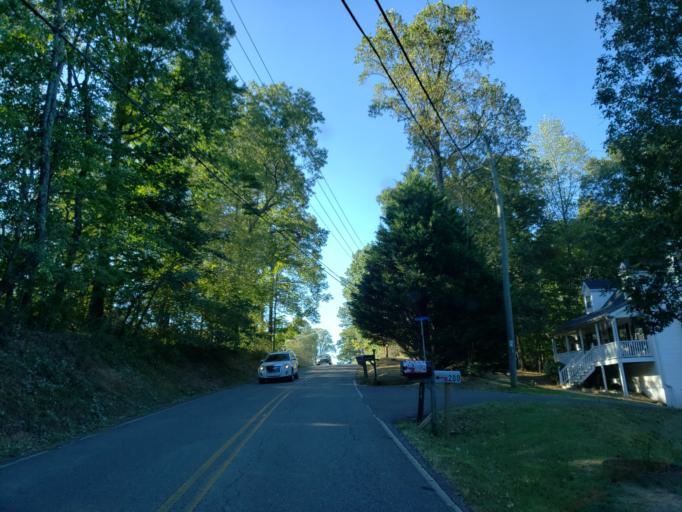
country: US
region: Georgia
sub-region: Pickens County
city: Nelson
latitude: 34.3721
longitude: -84.3840
